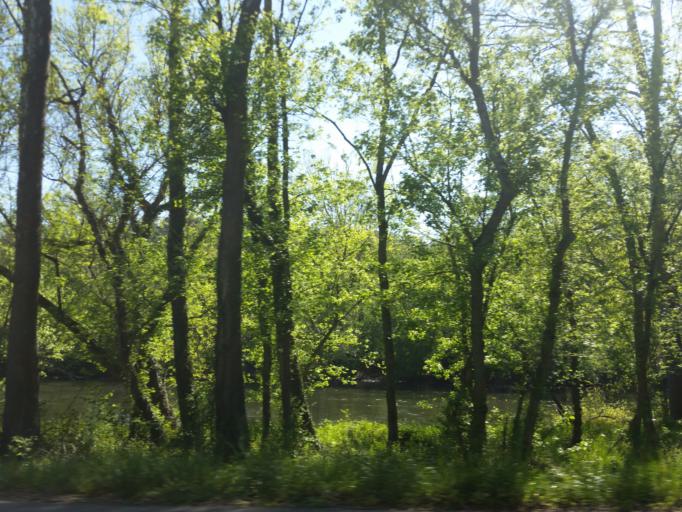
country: US
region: North Carolina
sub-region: Buncombe County
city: Asheville
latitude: 35.5733
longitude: -82.5648
